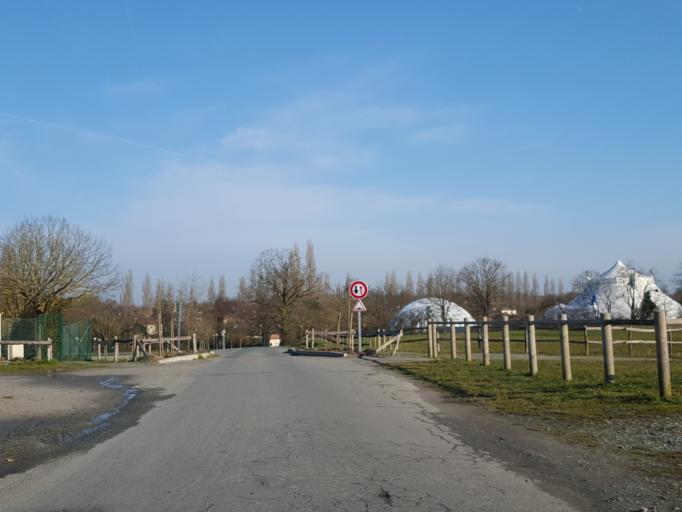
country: FR
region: Pays de la Loire
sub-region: Departement de la Vendee
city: La Chaize-le-Vicomte
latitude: 46.6696
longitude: -1.2860
